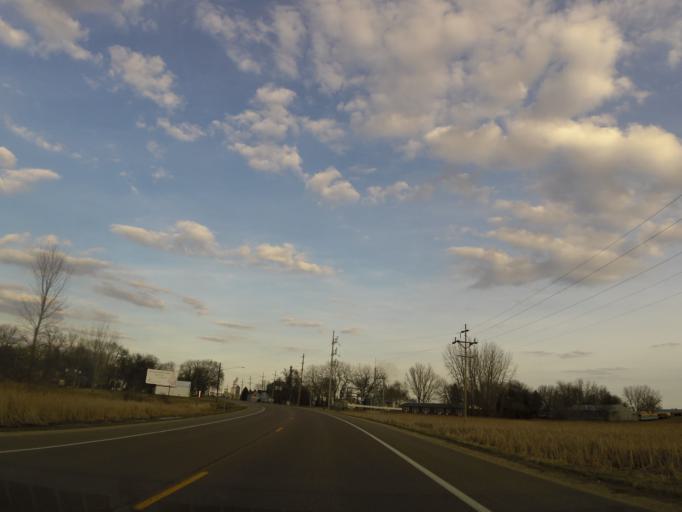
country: US
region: Minnesota
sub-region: McLeod County
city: Hutchinson
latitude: 44.7205
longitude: -94.4920
